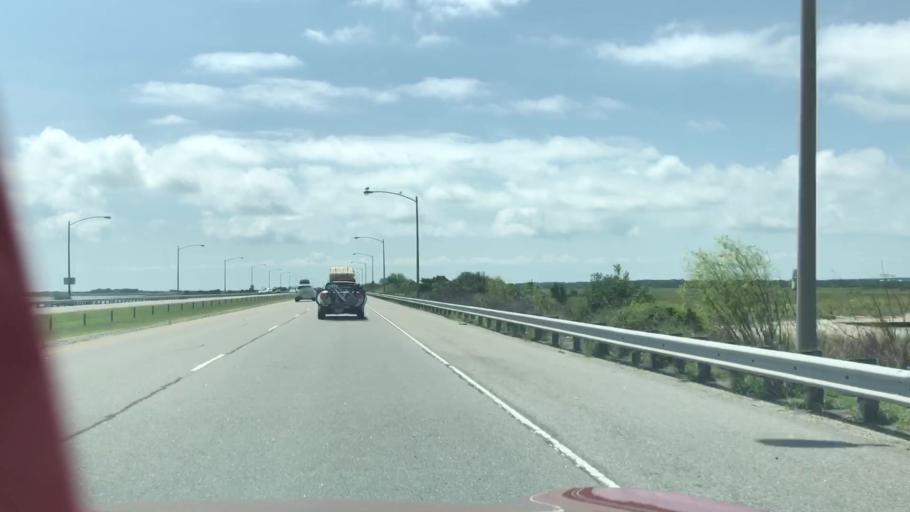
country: US
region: Virginia
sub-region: Northampton County
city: Cape Charles
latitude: 37.1104
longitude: -75.9694
